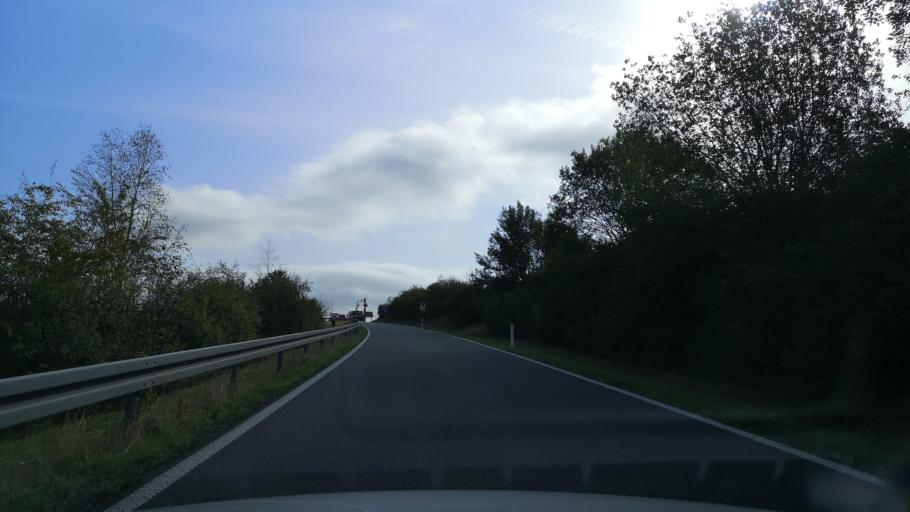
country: DE
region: North Rhine-Westphalia
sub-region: Regierungsbezirk Dusseldorf
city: Velbert
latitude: 51.3629
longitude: 7.0677
